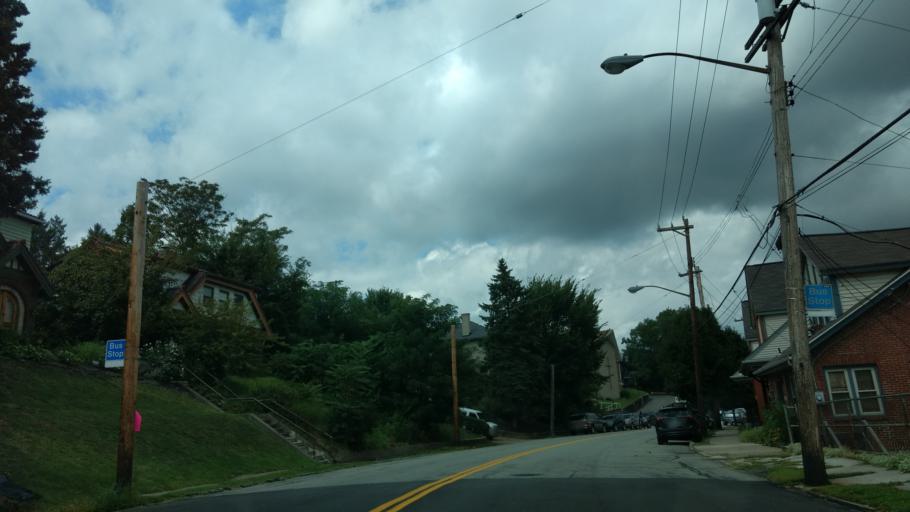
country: US
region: Pennsylvania
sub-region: Allegheny County
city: Millvale
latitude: 40.4760
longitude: -80.0123
